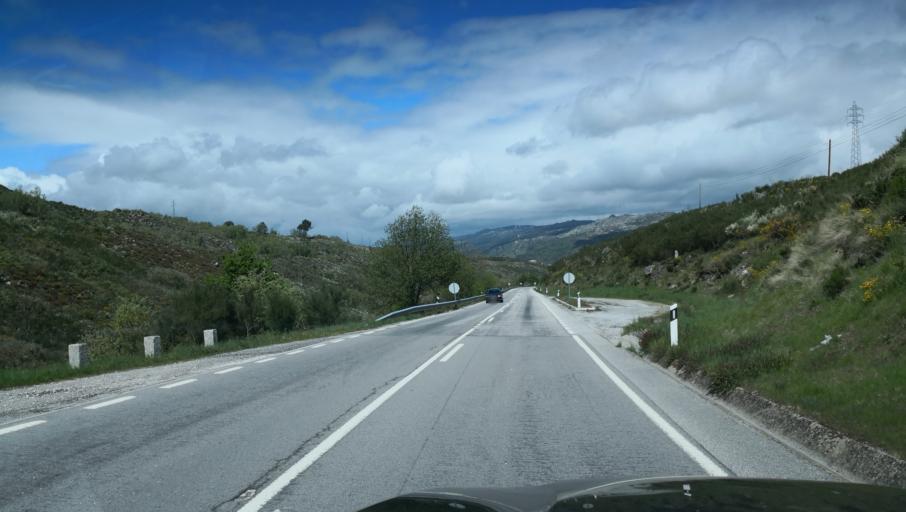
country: PT
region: Vila Real
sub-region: Vila Real
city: Vila Real
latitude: 41.4019
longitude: -7.6989
